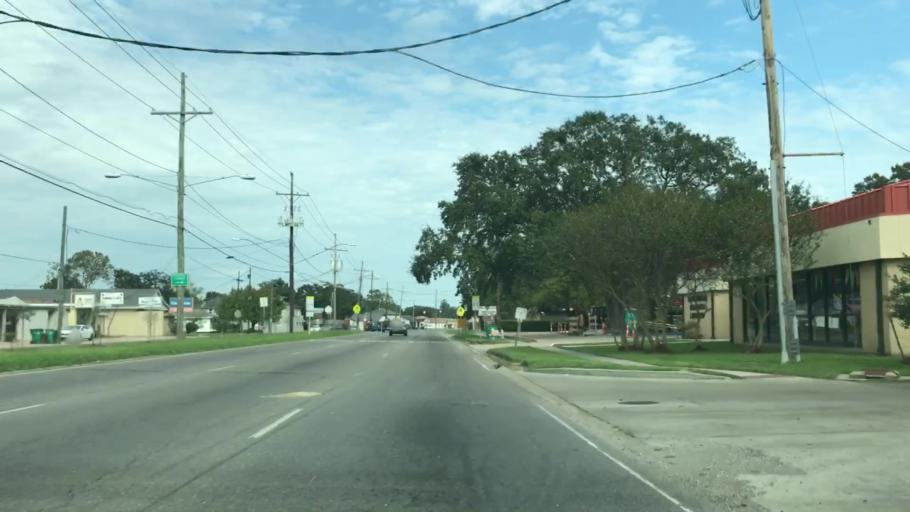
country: US
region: Louisiana
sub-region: Jefferson Parish
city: Jefferson
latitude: 29.9617
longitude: -90.1682
